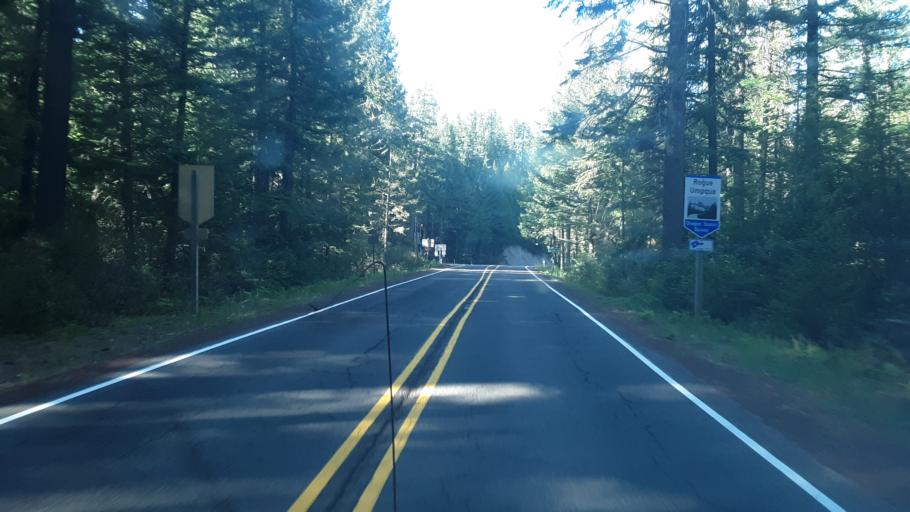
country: US
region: Oregon
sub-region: Jackson County
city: Shady Cove
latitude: 42.9223
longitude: -122.4289
